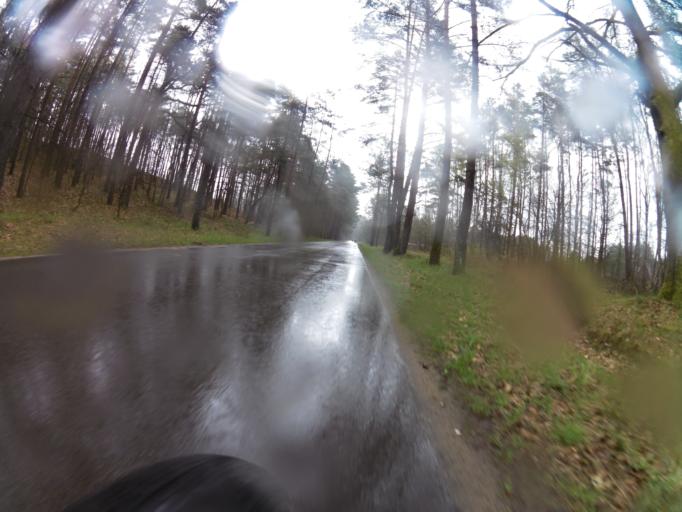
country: PL
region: Pomeranian Voivodeship
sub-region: Powiat slupski
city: Kepice
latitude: 54.2844
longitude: 16.8230
